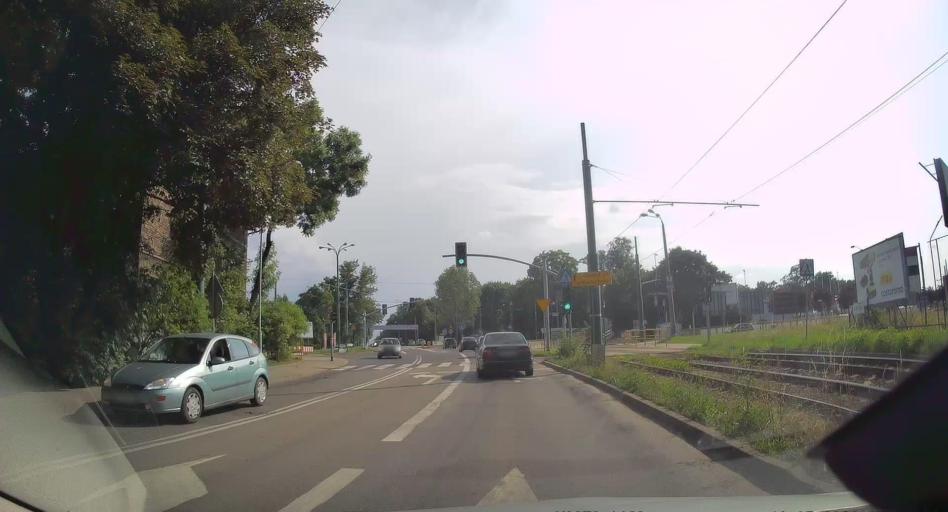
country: PL
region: Silesian Voivodeship
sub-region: Swietochlowice
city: Swietochlowice
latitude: 50.3056
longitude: 18.9198
